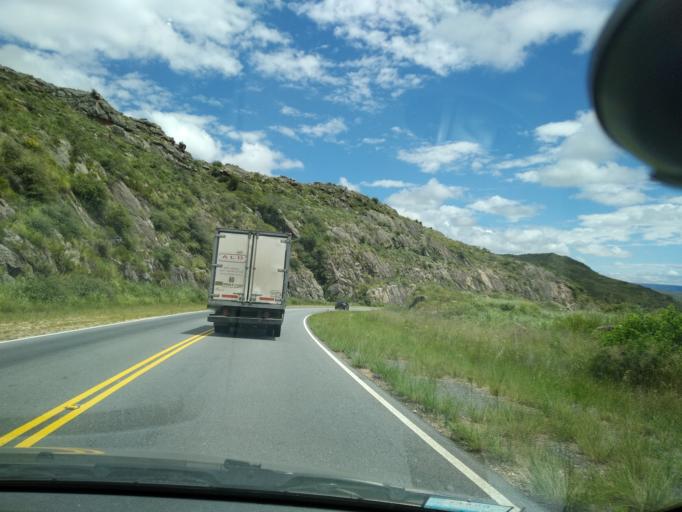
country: AR
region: Cordoba
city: Cuesta Blanca
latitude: -31.6152
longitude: -64.6722
